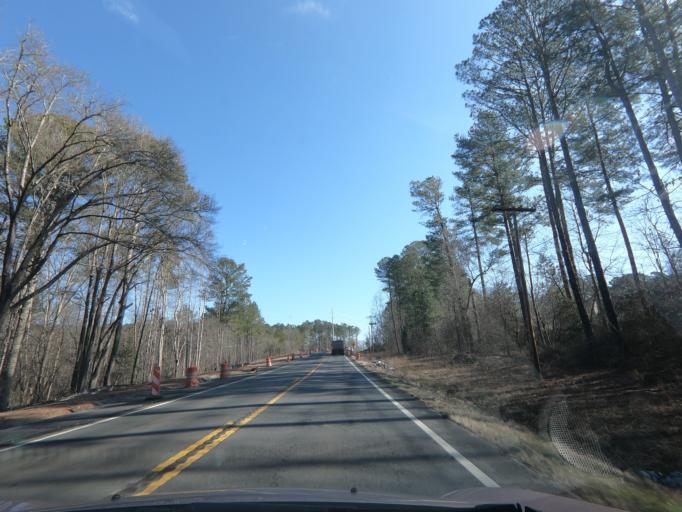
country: US
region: Georgia
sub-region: Forsyth County
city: Cumming
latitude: 34.3052
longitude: -84.2174
